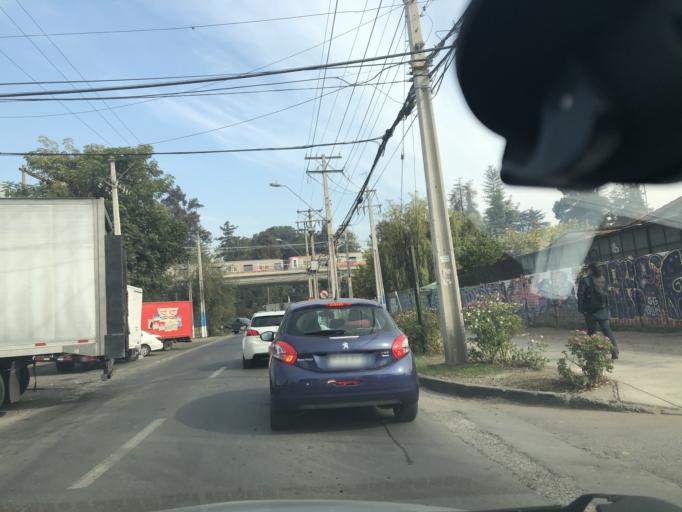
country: CL
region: Santiago Metropolitan
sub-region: Provincia de Cordillera
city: Puente Alto
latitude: -33.5805
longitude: -70.5806
